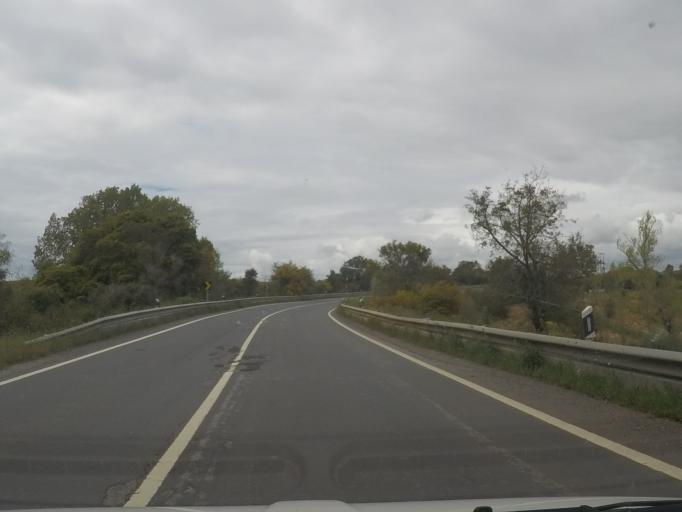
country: PT
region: Setubal
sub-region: Santiago do Cacem
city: Cercal
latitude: 37.8364
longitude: -8.7040
